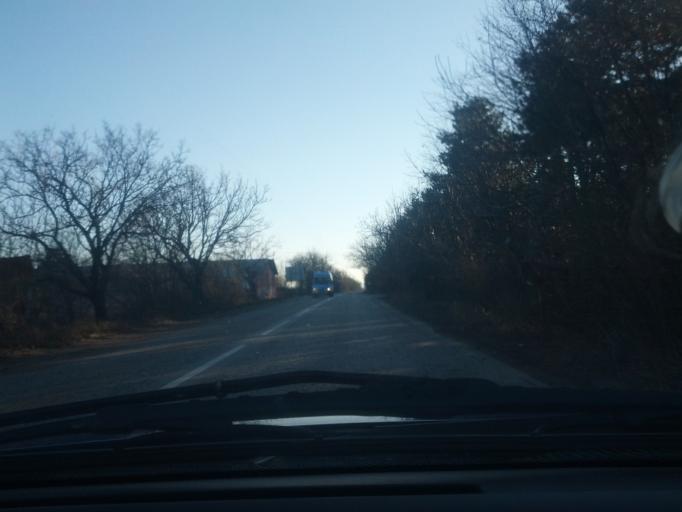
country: BG
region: Vratsa
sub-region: Obshtina Borovan
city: Borovan
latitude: 43.4895
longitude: 23.7959
